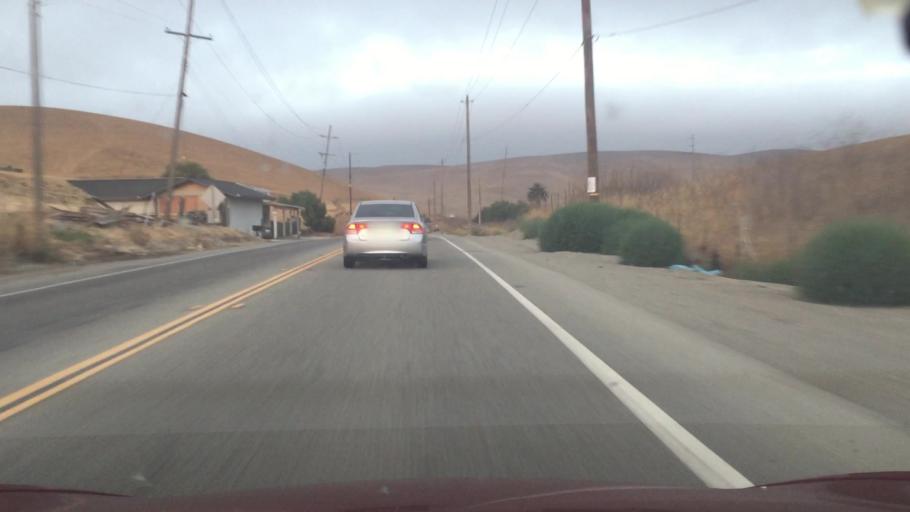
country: US
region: California
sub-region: Alameda County
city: Livermore
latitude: 37.7442
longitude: -121.6614
